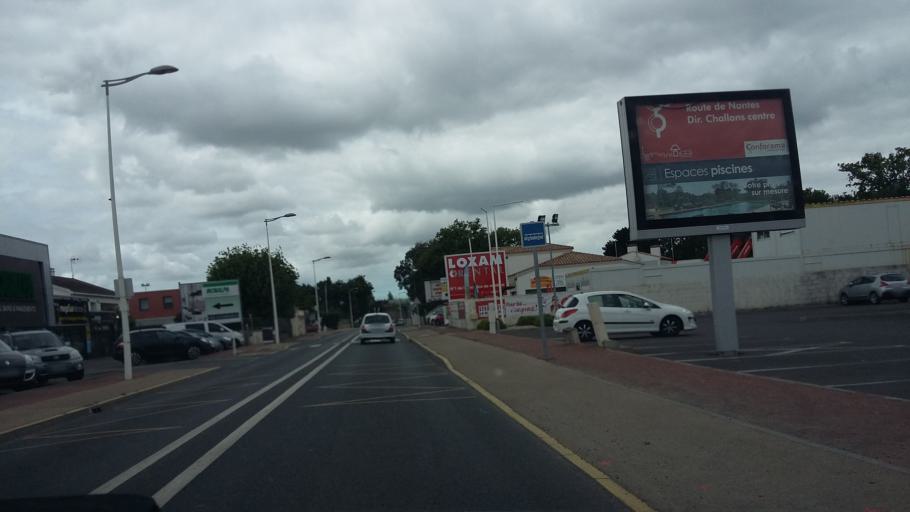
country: FR
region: Pays de la Loire
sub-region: Departement de la Vendee
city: Challans
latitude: 46.8536
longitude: -1.8938
